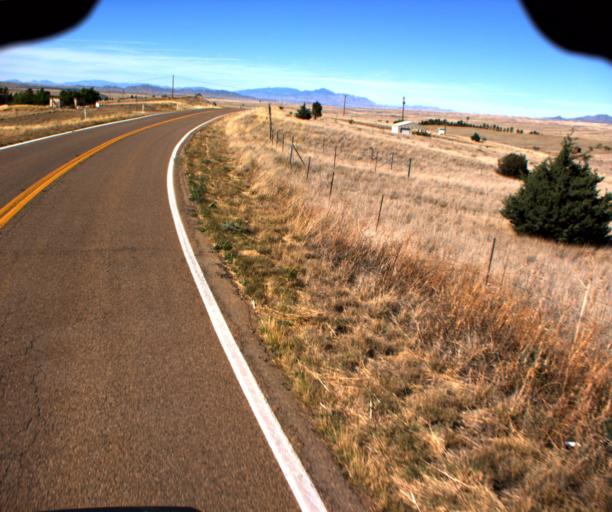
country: US
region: Arizona
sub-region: Cochise County
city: Huachuca City
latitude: 31.6645
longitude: -110.6055
